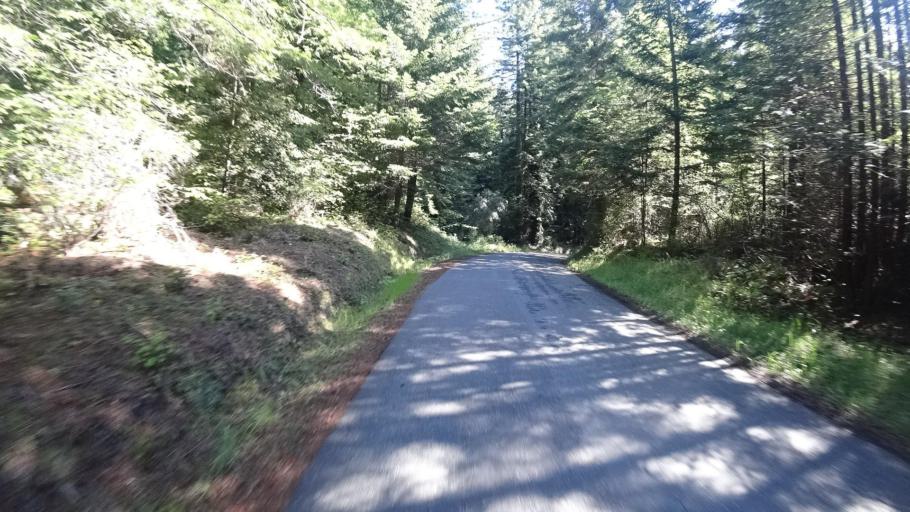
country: US
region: California
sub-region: Humboldt County
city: Rio Dell
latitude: 40.4584
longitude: -124.0160
